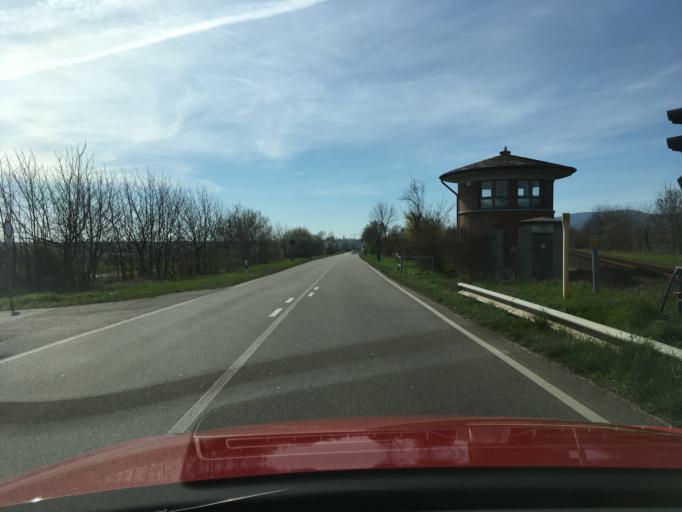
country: DE
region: Rheinland-Pfalz
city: Deidesheim
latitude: 49.3929
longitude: 8.1818
